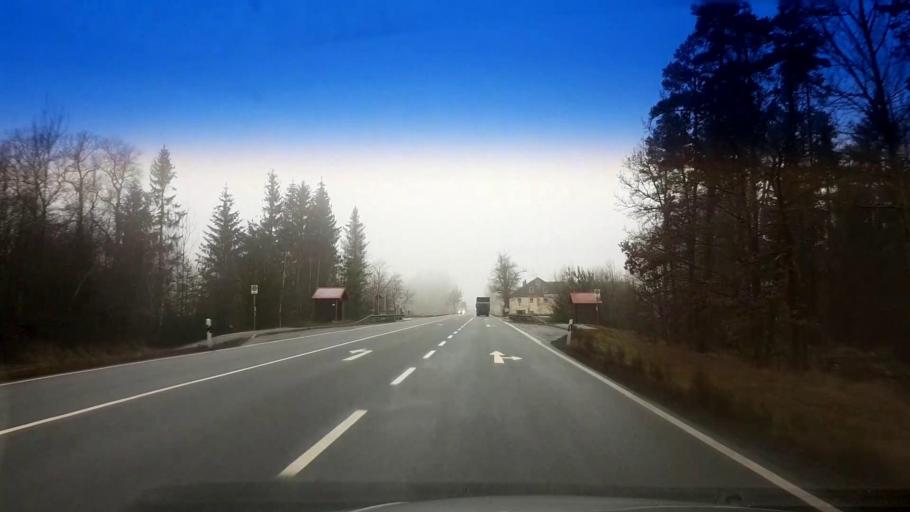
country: DE
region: Bavaria
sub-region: Upper Palatinate
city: Leonberg
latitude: 49.9266
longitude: 12.2810
